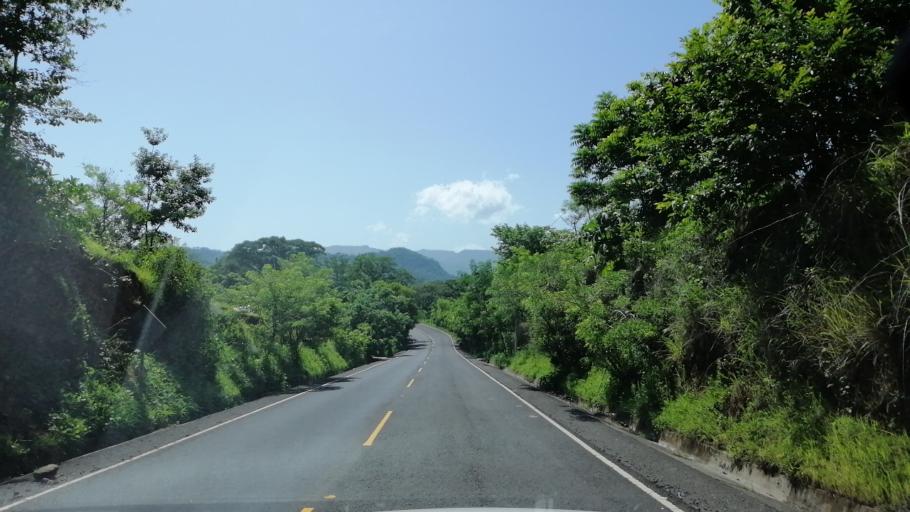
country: HN
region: Lempira
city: La Virtud
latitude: 13.9572
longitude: -88.7620
